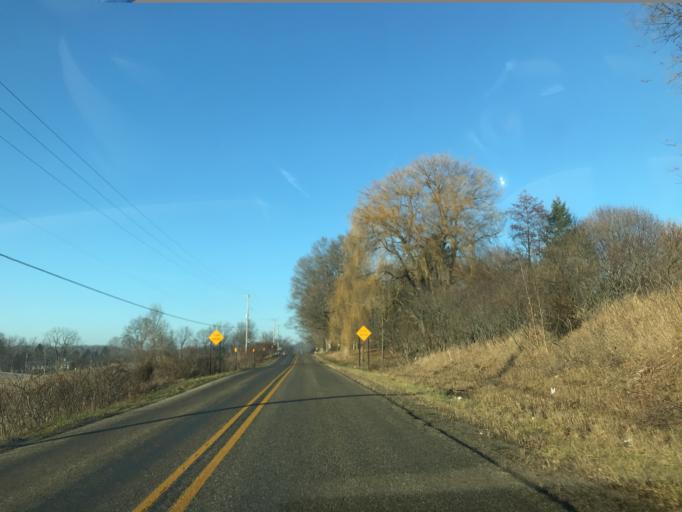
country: US
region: Michigan
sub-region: Eaton County
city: Dimondale
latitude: 42.6619
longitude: -84.6388
